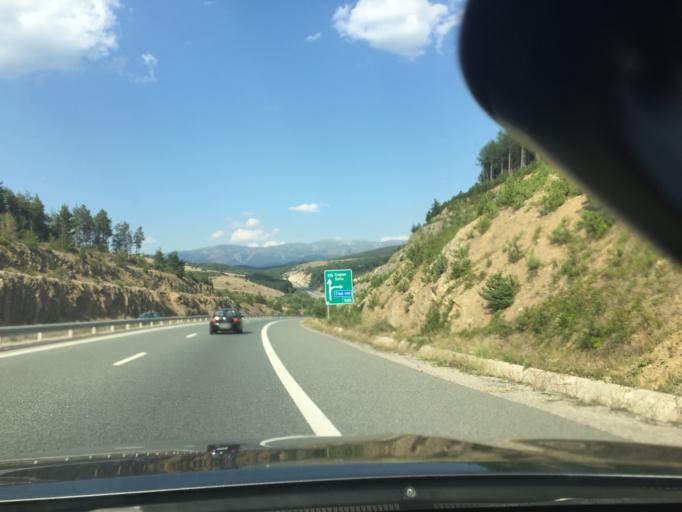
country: BG
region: Pernik
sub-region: Obshtina Pernik
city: Pernik
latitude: 42.4810
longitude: 23.1139
